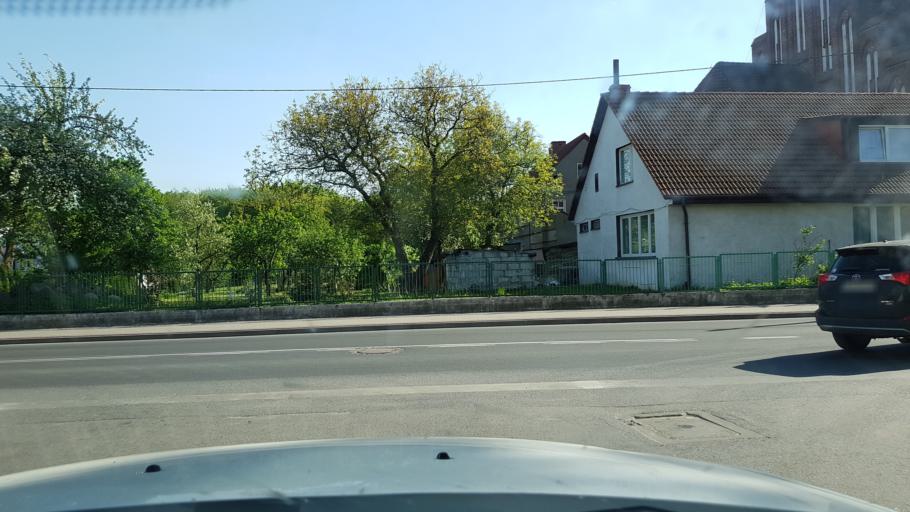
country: PL
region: West Pomeranian Voivodeship
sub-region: Powiat lobeski
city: Resko
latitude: 53.7731
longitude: 15.4074
